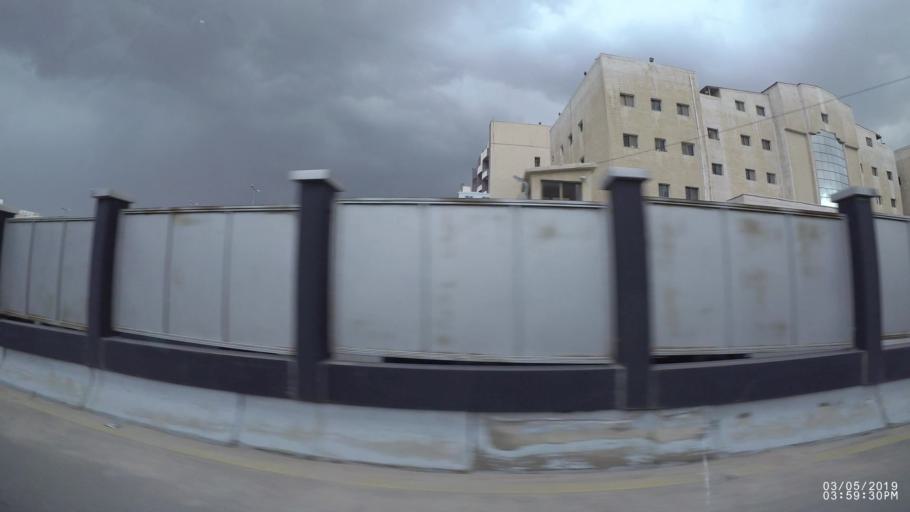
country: JO
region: Amman
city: Amman
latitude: 32.0114
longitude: 35.9569
